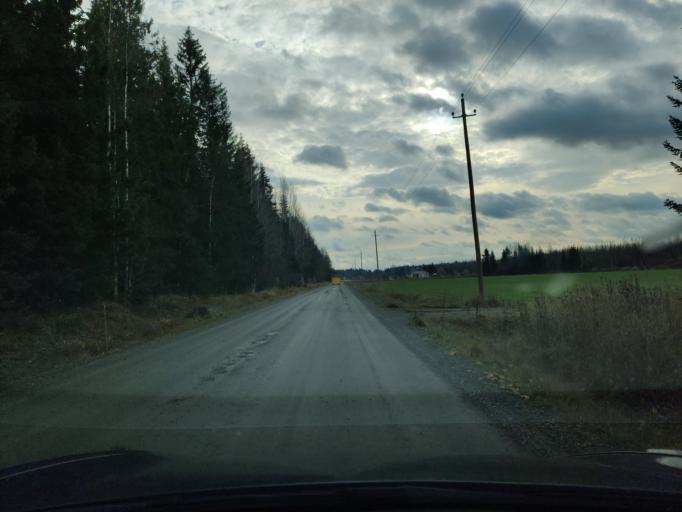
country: FI
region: Northern Savo
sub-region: Kuopio
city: Siilinjaervi
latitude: 63.1097
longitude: 27.5531
